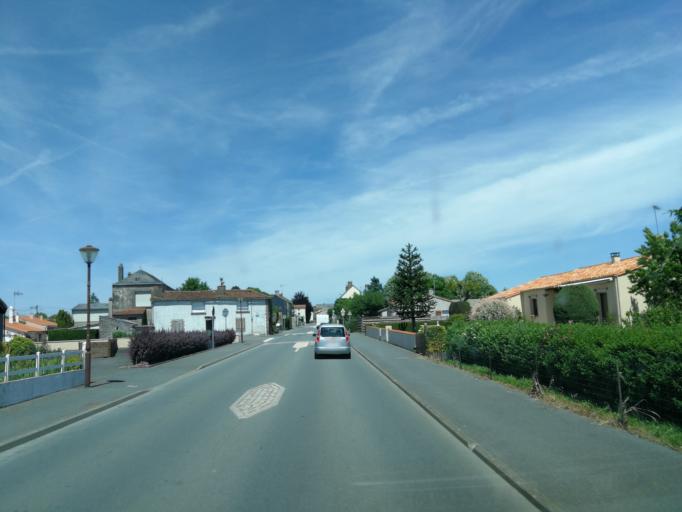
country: FR
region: Pays de la Loire
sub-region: Departement de la Vendee
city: Saint-Pierre-du-Chemin
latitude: 46.6930
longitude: -0.7038
